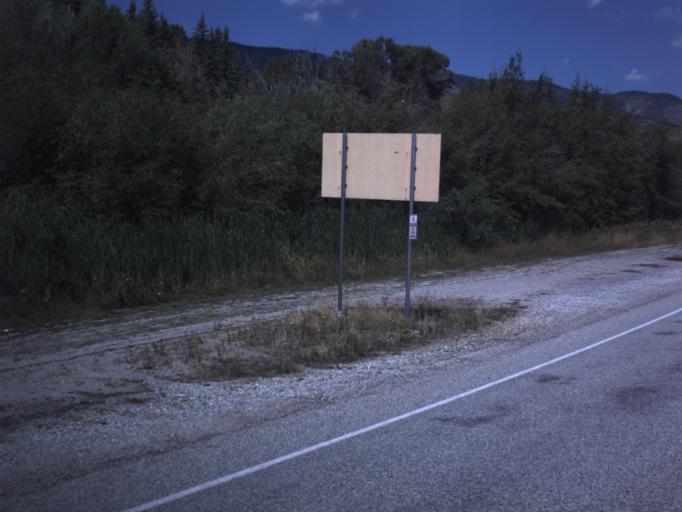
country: US
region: Idaho
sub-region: Bear Lake County
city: Paris
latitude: 41.9670
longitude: -111.3996
